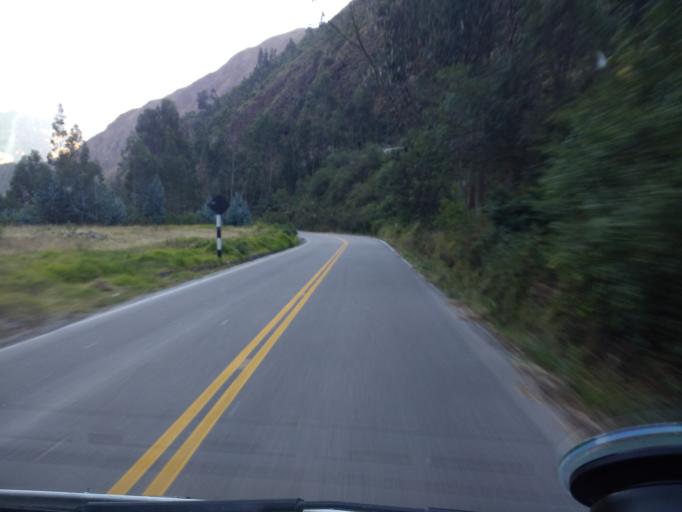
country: PE
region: Cusco
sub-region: Provincia de Urubamba
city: Ollantaytambo
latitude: -13.2007
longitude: -72.2954
